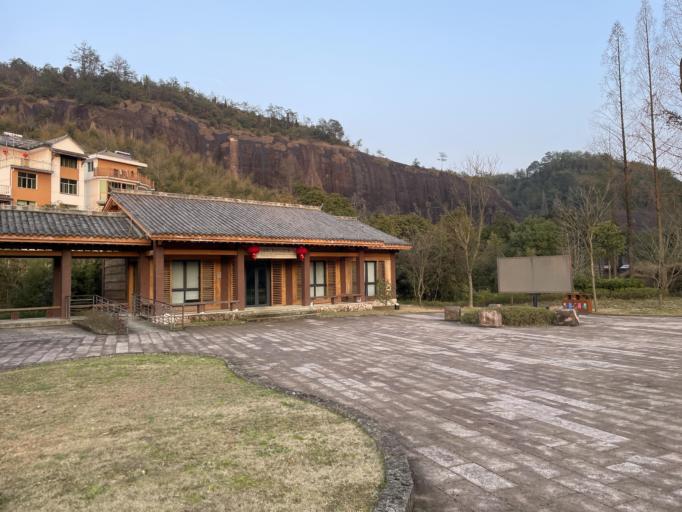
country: CN
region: Zhejiang Sheng
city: Shuhong
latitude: 28.6896
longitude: 120.1243
